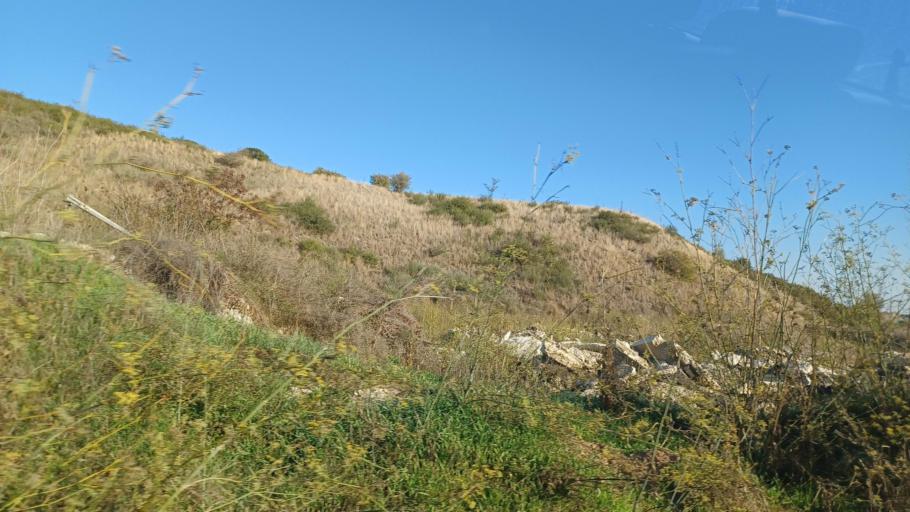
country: CY
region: Pafos
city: Polis
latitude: 35.0064
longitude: 32.4282
